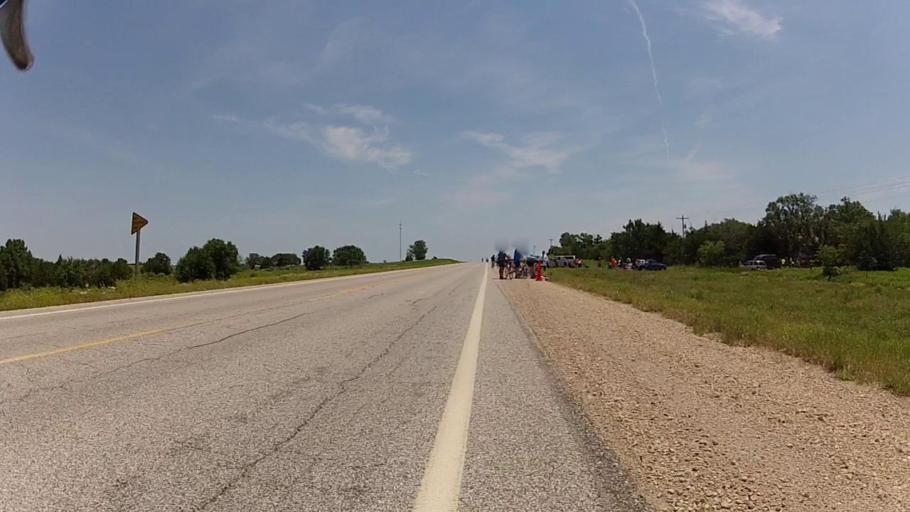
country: US
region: Kansas
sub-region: Chautauqua County
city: Sedan
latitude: 37.1132
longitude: -96.3200
